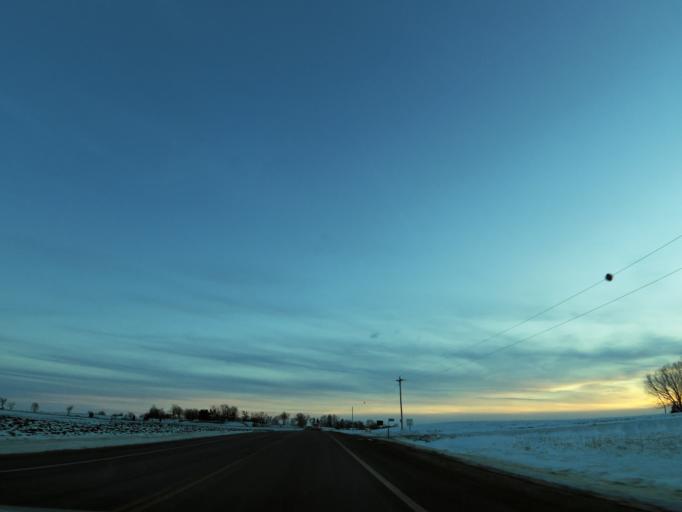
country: US
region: Minnesota
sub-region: Carver County
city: Chaska
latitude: 44.7373
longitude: -93.5622
